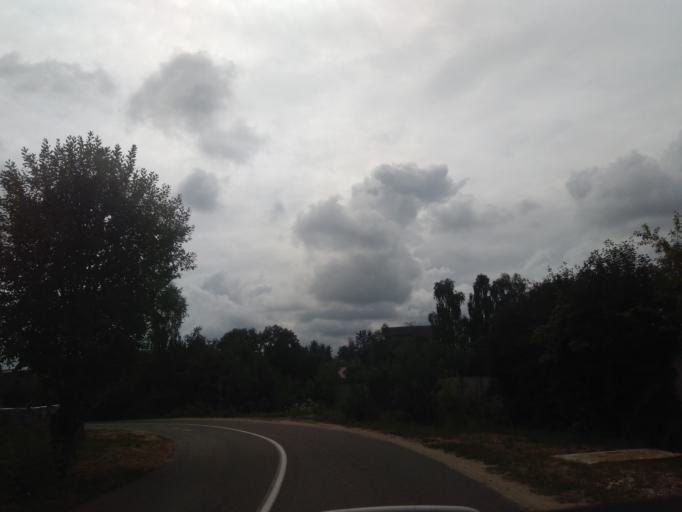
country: BY
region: Minsk
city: Slabada
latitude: 53.9839
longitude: 27.9016
